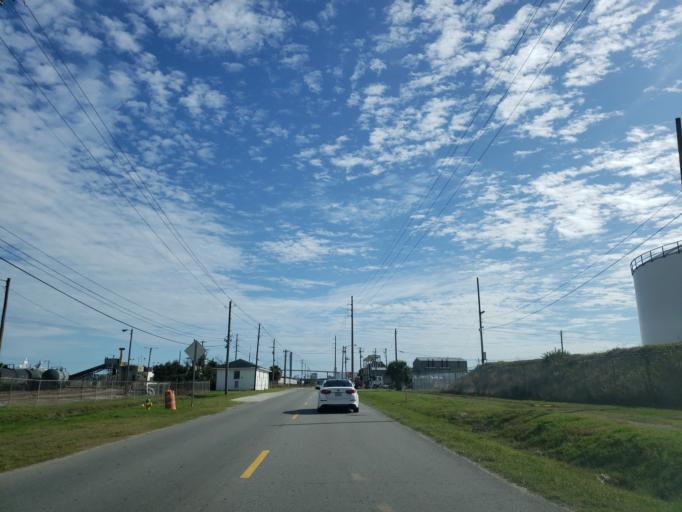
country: US
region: Georgia
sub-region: Chatham County
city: Savannah
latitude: 32.0983
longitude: -81.1185
